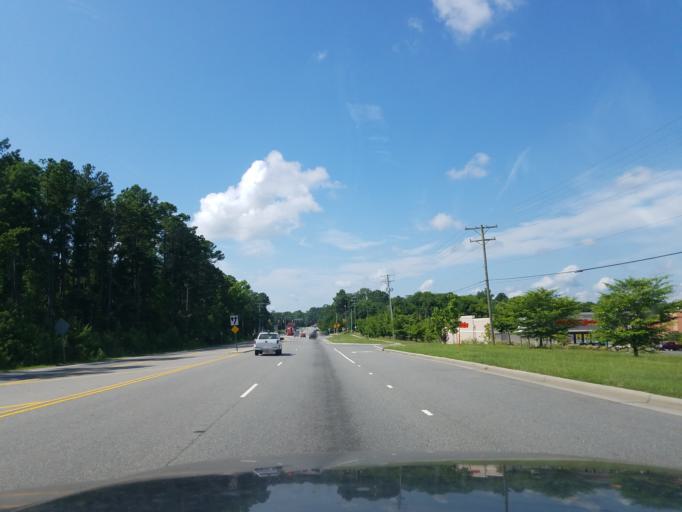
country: US
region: North Carolina
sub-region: Durham County
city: Durham
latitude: 35.9416
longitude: -78.9061
